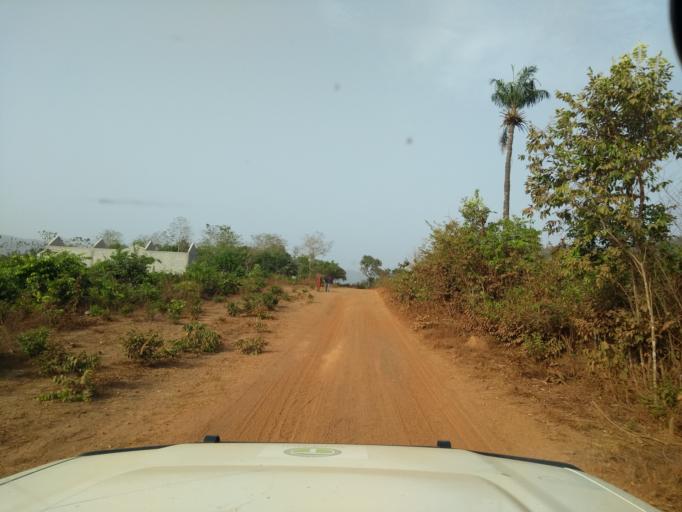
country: GN
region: Kindia
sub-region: Prefecture de Dubreka
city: Dubreka
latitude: 9.8532
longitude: -13.5528
